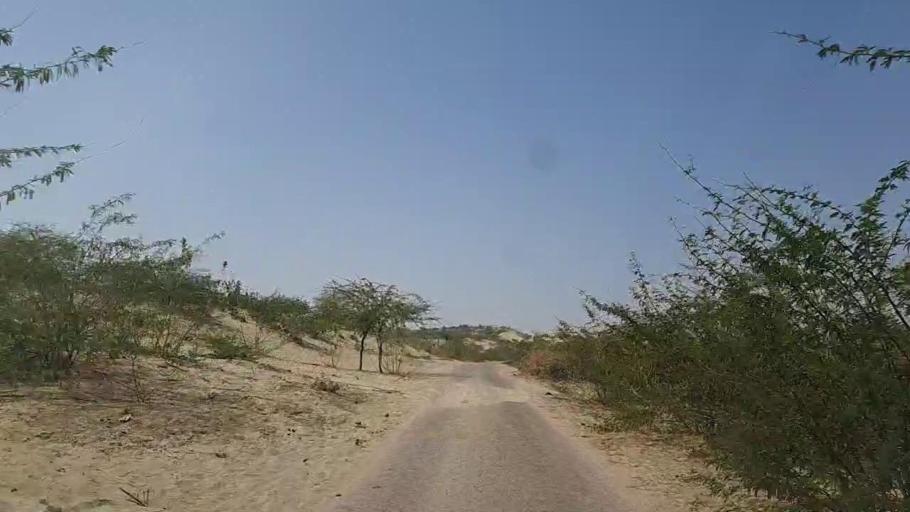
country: PK
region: Sindh
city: Diplo
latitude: 24.5247
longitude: 69.3671
